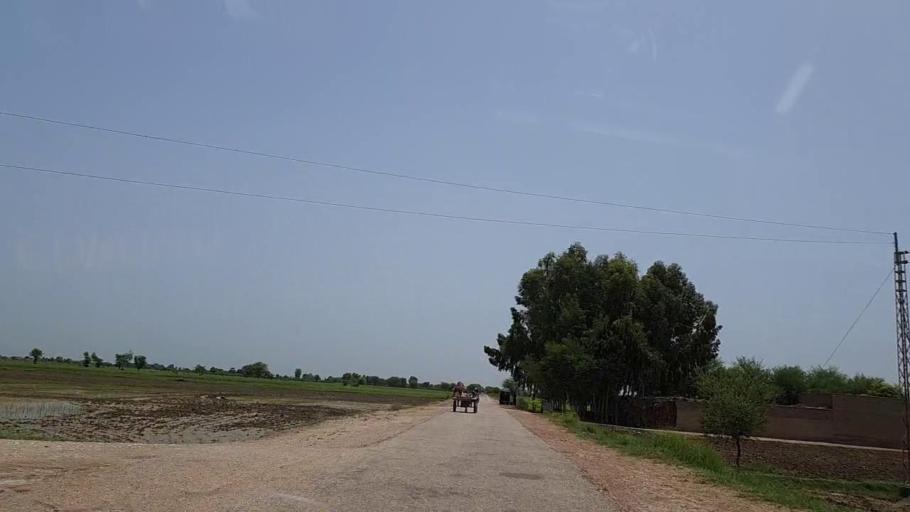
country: PK
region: Sindh
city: Tharu Shah
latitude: 26.9617
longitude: 68.0597
